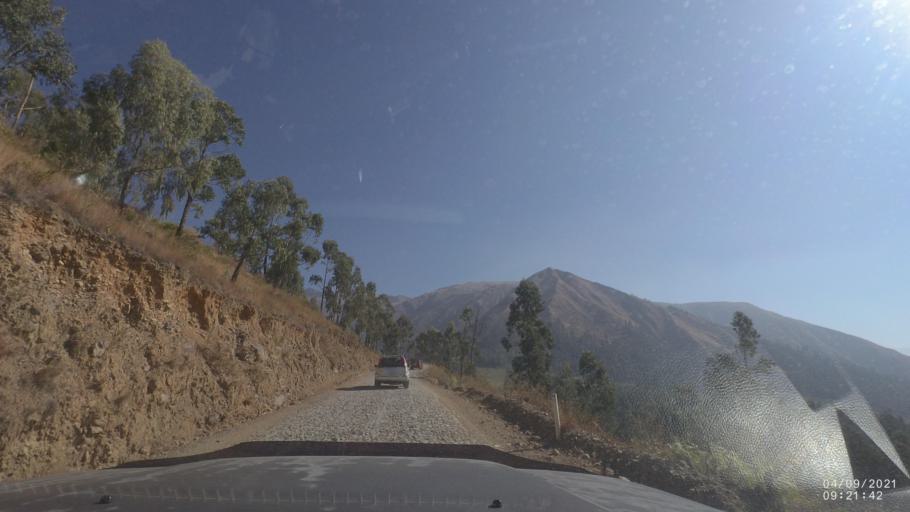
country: BO
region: Cochabamba
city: Sipe Sipe
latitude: -17.3636
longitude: -66.3655
